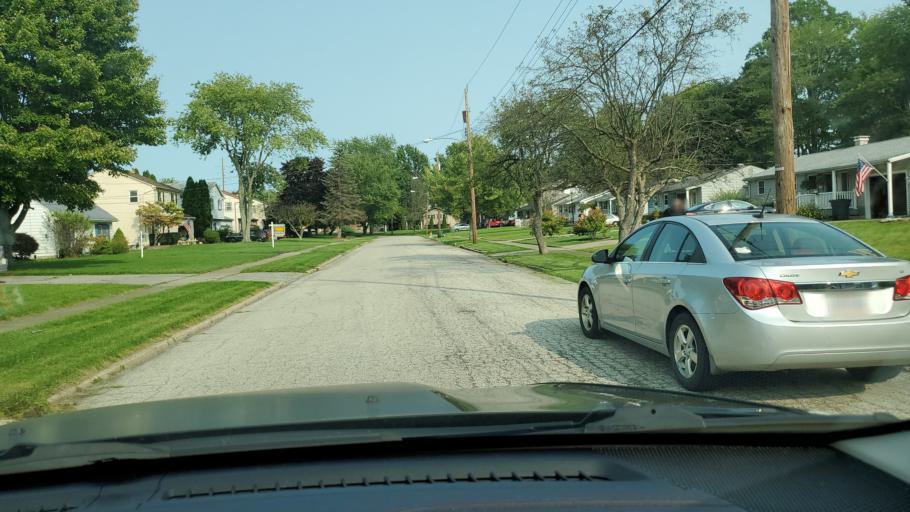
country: US
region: Ohio
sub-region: Mahoning County
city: Poland
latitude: 41.0363
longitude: -80.6241
